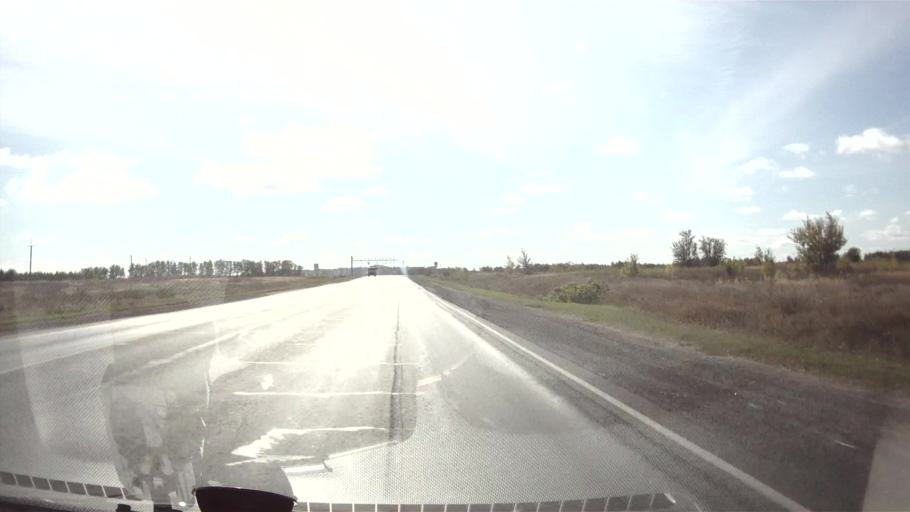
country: RU
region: Ulyanovsk
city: Isheyevka
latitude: 54.3010
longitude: 48.2451
